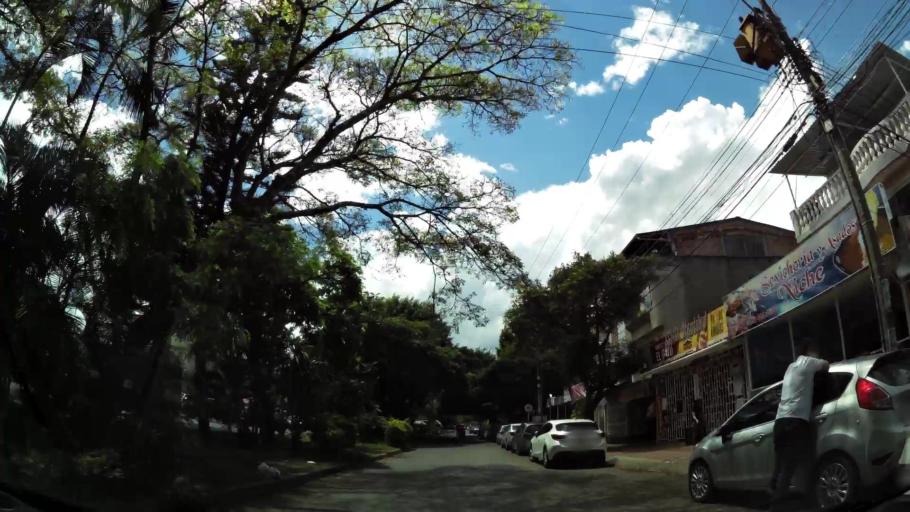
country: CO
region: Valle del Cauca
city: Cali
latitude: 3.3838
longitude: -76.5212
